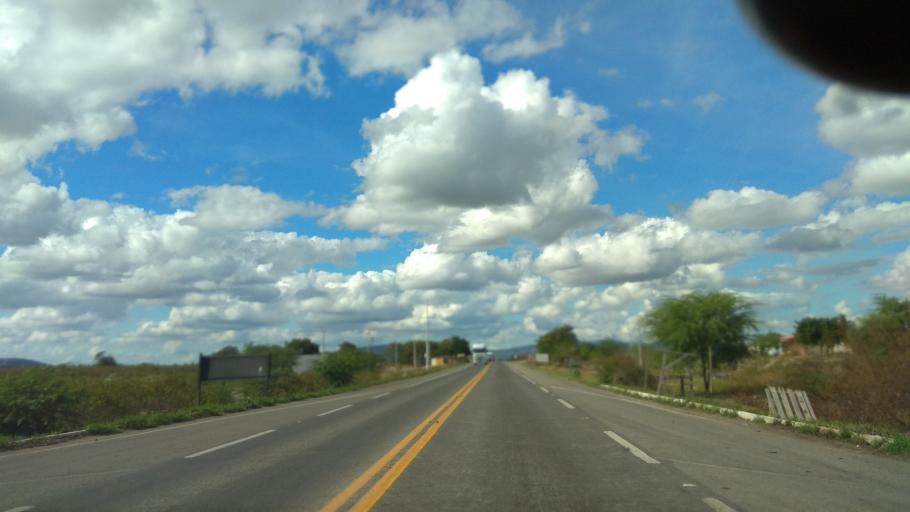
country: BR
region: Bahia
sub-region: Castro Alves
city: Castro Alves
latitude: -12.7047
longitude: -39.7215
